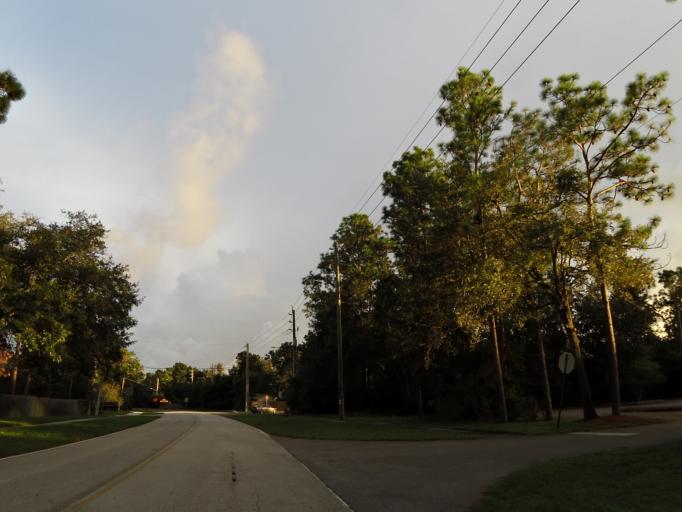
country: US
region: Florida
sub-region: Duval County
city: Atlantic Beach
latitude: 30.3624
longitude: -81.4830
